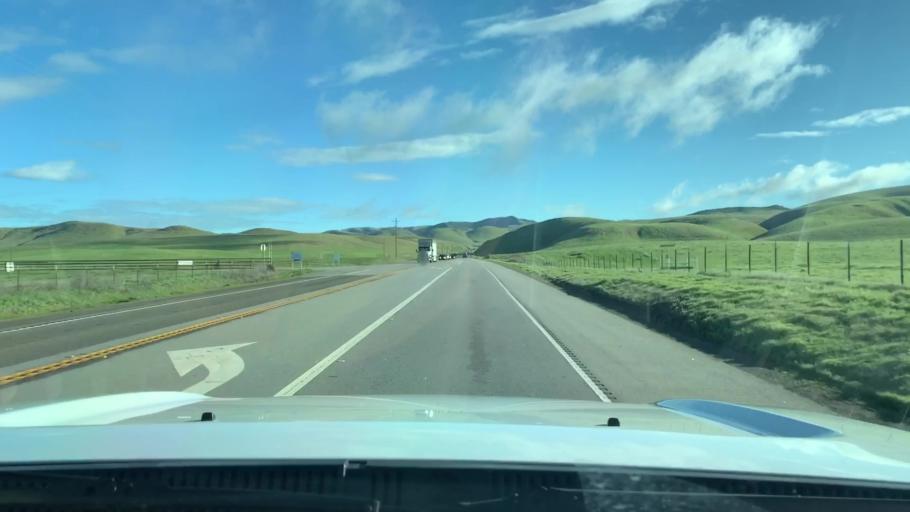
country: US
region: California
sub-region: San Luis Obispo County
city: Shandon
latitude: 35.7451
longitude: -120.2729
